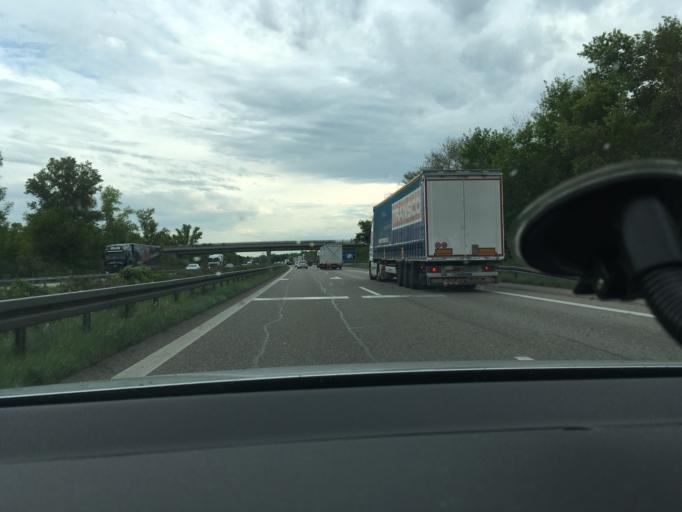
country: FR
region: Alsace
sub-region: Departement du Haut-Rhin
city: Blodelsheim
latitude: 47.8798
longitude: 7.5731
